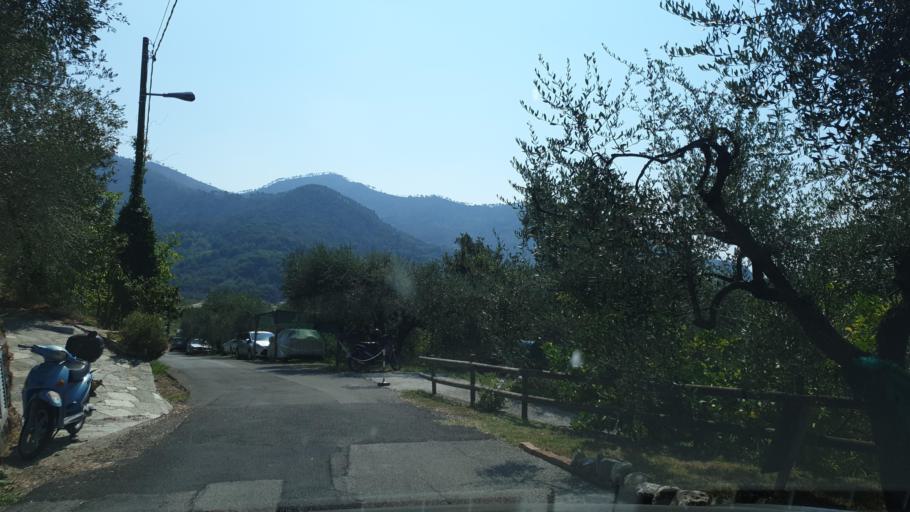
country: IT
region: Liguria
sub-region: Provincia di La Spezia
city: Levanto
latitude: 44.1802
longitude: 9.6184
